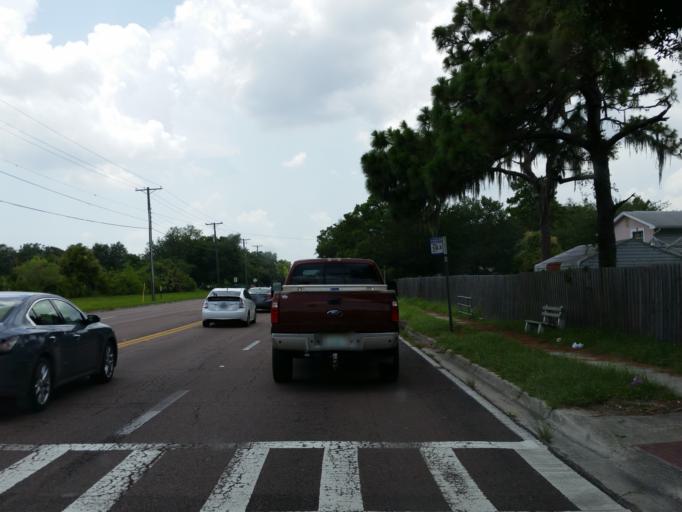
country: US
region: Florida
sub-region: Hillsborough County
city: Brandon
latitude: 27.8937
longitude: -82.2878
